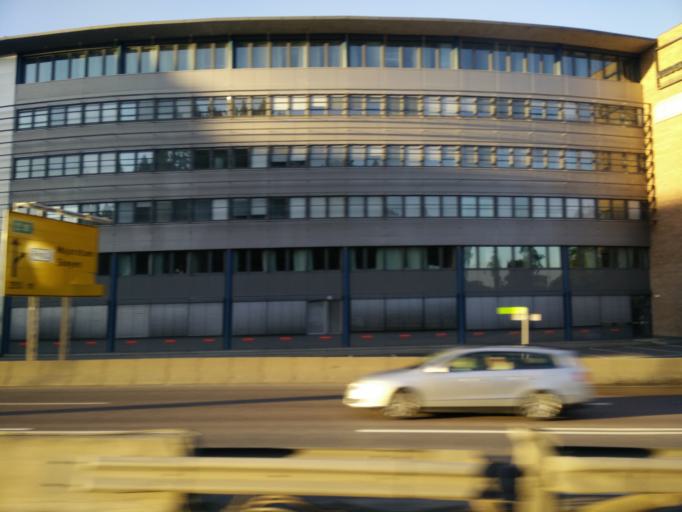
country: NO
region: Oslo
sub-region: Oslo
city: Sjolyststranda
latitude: 59.9194
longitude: 10.6816
